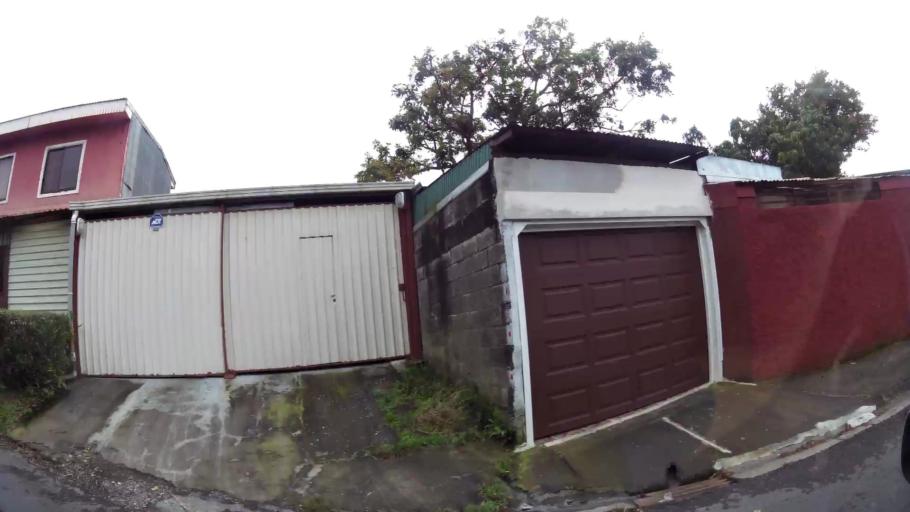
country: CR
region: San Jose
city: Ipis
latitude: 9.9704
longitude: -84.0234
